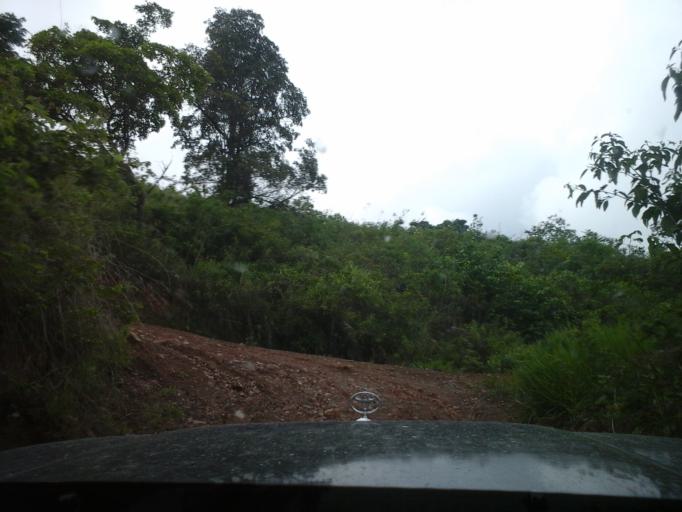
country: CO
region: Cesar
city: Agustin Codazzi
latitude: 9.9537
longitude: -73.0680
